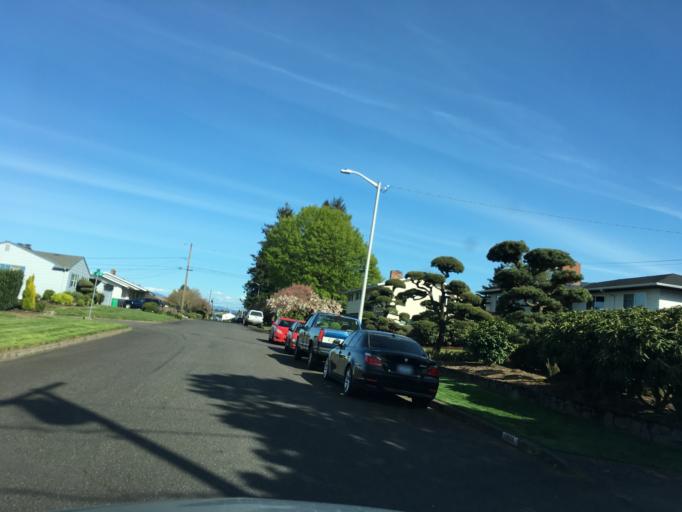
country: US
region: Oregon
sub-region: Multnomah County
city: Lents
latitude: 45.5457
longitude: -122.5278
